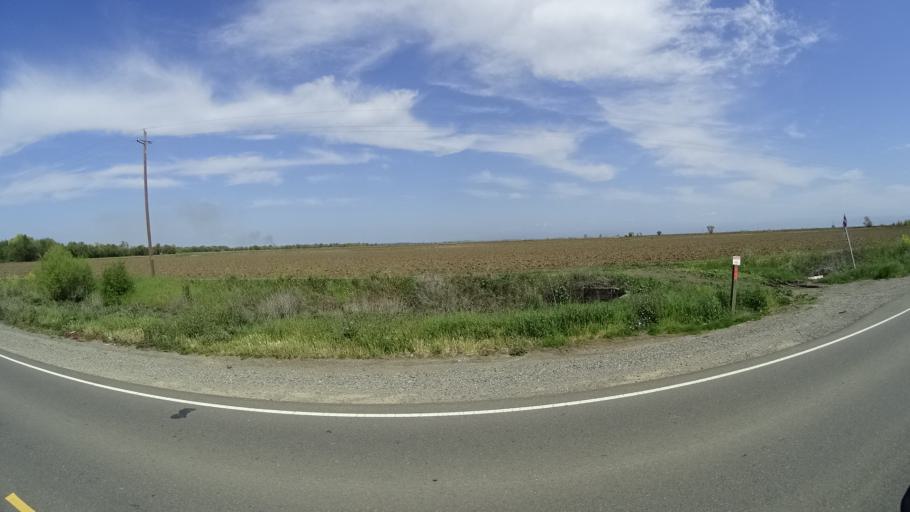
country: US
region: California
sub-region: Butte County
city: Biggs
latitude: 39.4641
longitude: -121.8632
